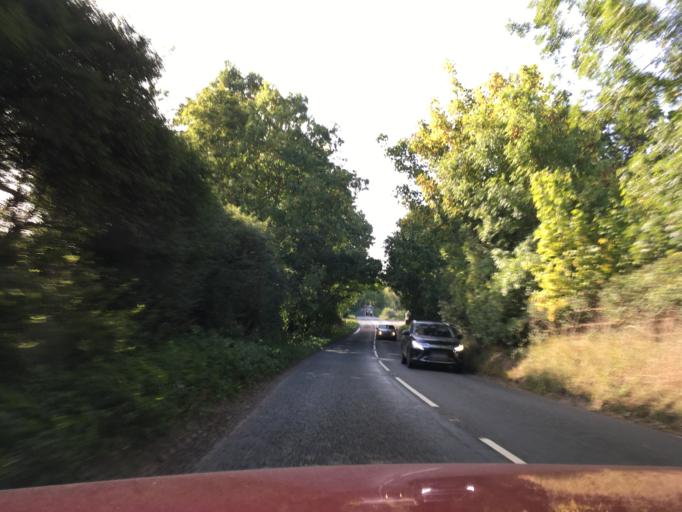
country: GB
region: England
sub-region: Gloucestershire
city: Tewkesbury
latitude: 51.9453
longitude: -2.2134
